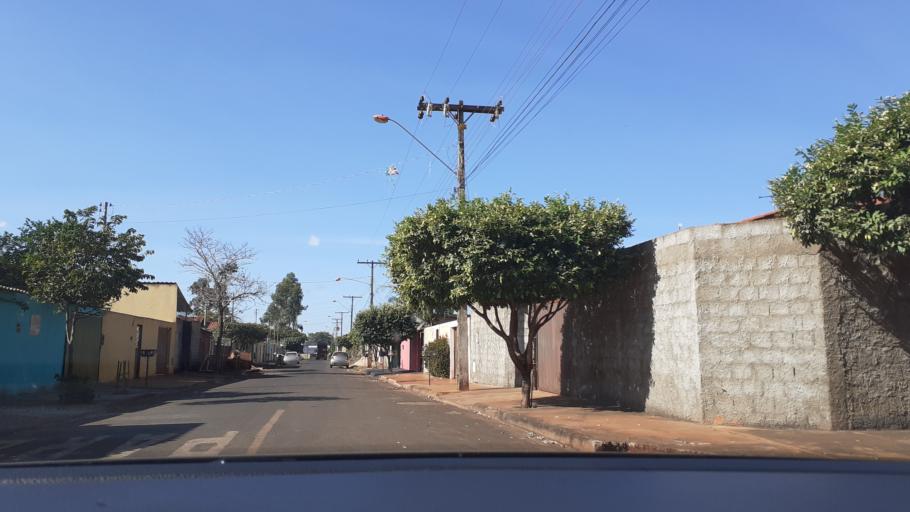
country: BR
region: Goias
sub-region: Itumbiara
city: Itumbiara
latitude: -18.4125
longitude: -49.2535
